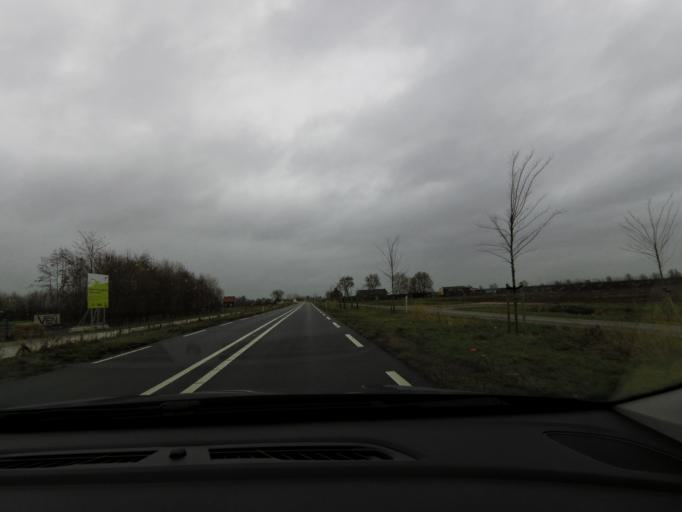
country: NL
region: North Brabant
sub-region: Gemeente Waalwijk
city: Waspik
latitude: 51.7313
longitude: 4.9272
